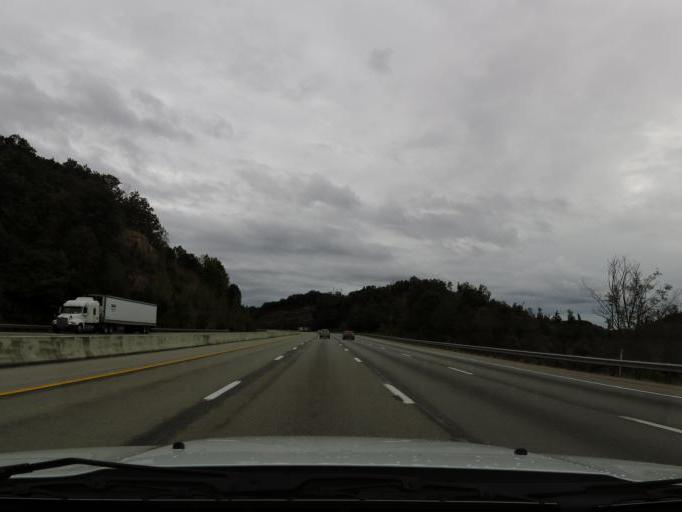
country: US
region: Kentucky
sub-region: Rockcastle County
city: Mount Vernon
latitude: 37.2717
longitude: -84.2526
